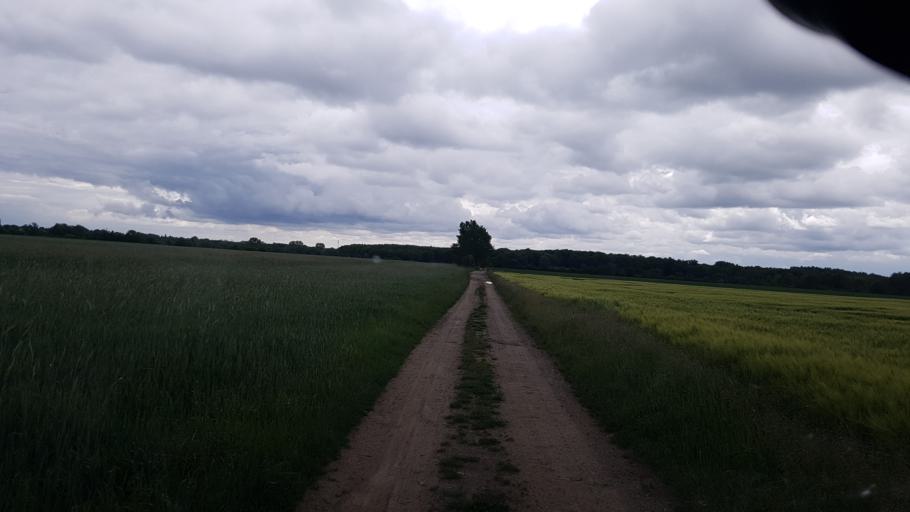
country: DE
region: Brandenburg
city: Doberlug-Kirchhain
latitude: 51.6310
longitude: 13.5394
